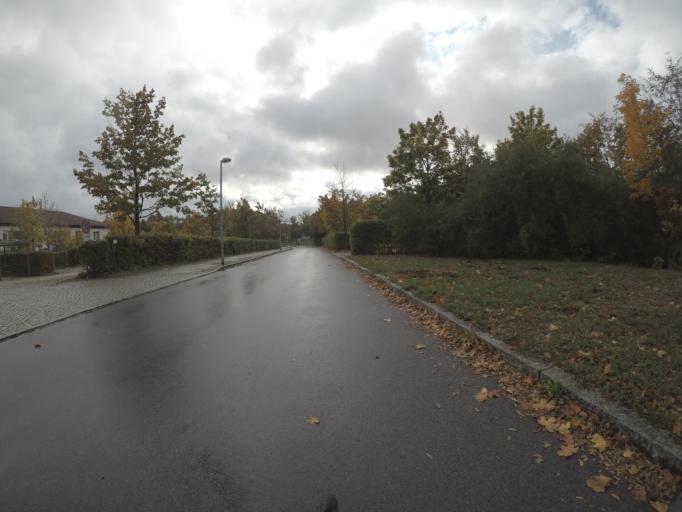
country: DE
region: Berlin
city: Blankenfelde
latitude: 52.6591
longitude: 13.3854
